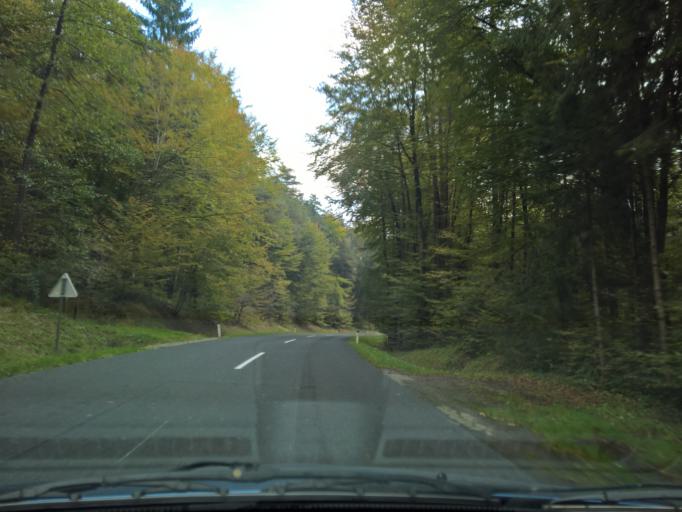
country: AT
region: Styria
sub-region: Politischer Bezirk Deutschlandsberg
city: Unterbergla
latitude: 46.7970
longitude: 15.3346
